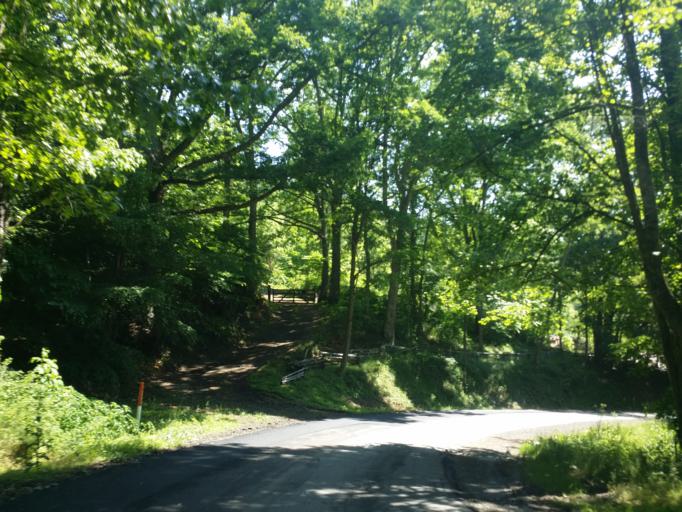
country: US
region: North Carolina
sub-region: Haywood County
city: Cove Creek
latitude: 35.7733
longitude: -82.8929
